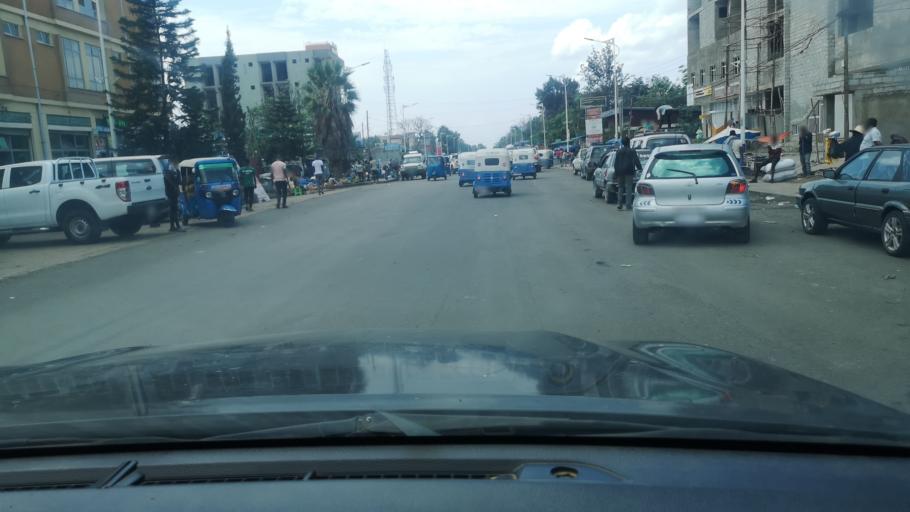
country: ET
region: Oromiya
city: Waliso
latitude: 8.2819
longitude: 37.7784
